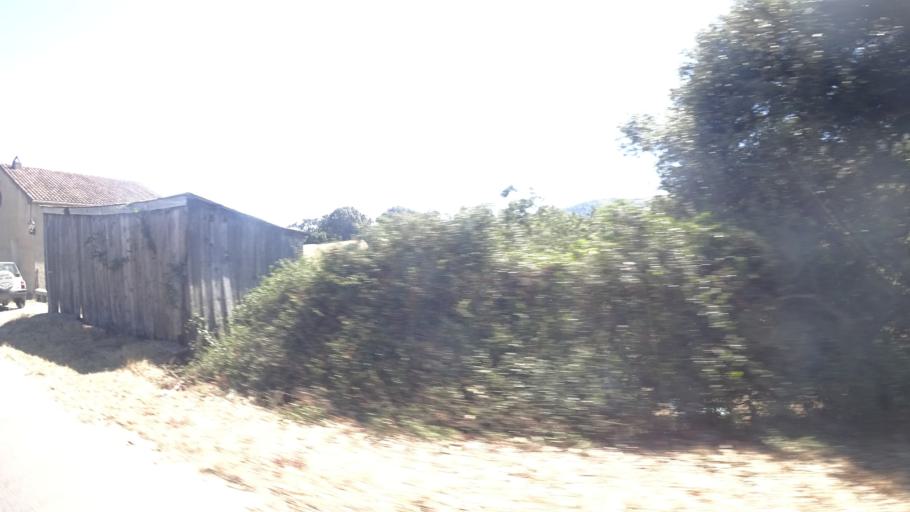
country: FR
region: Corsica
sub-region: Departement de la Corse-du-Sud
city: Alata
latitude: 41.9552
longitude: 8.7296
